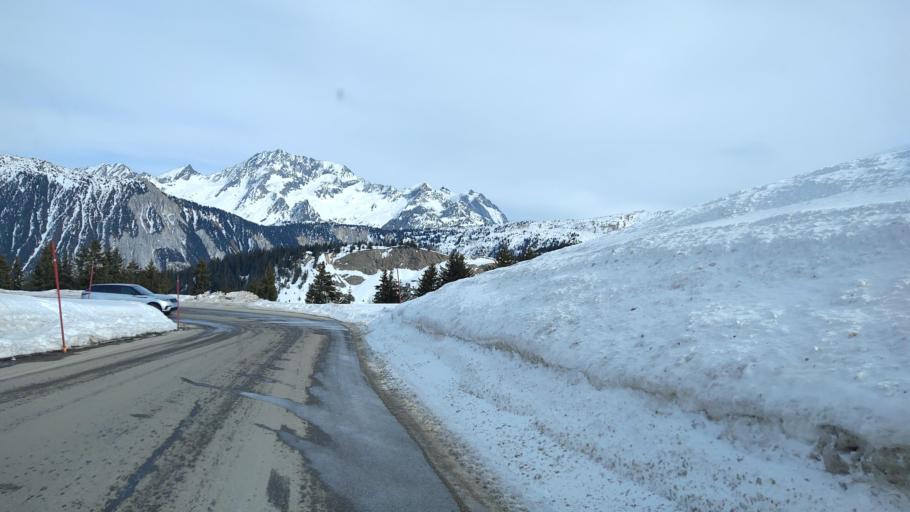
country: FR
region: Rhone-Alpes
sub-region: Departement de la Savoie
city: Courchevel
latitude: 45.4001
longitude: 6.6370
